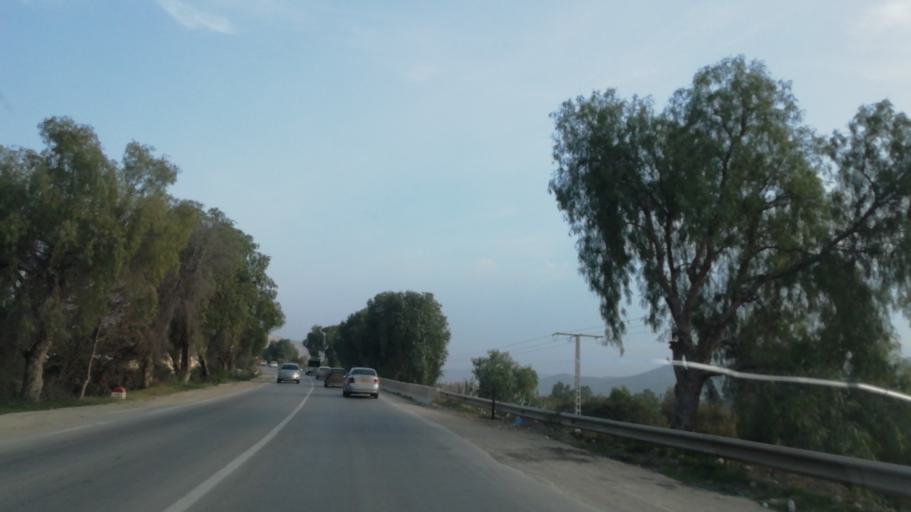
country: DZ
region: Mascara
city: Bou Hanifia el Hamamat
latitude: 35.4672
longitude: -0.0075
